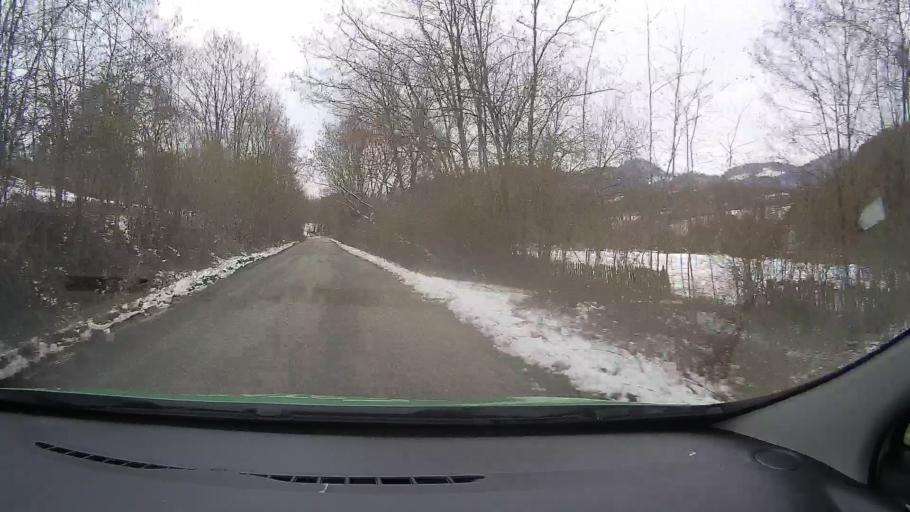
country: RO
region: Hunedoara
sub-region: Comuna Balsa
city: Balsa
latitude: 46.0391
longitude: 23.0748
